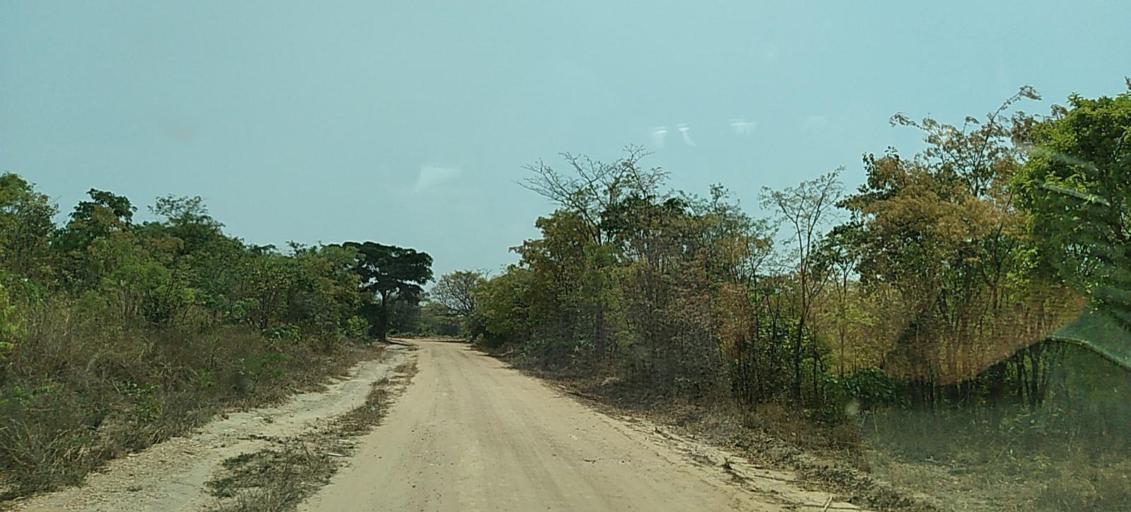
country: ZM
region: Copperbelt
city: Kalulushi
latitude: -12.9399
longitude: 28.1595
